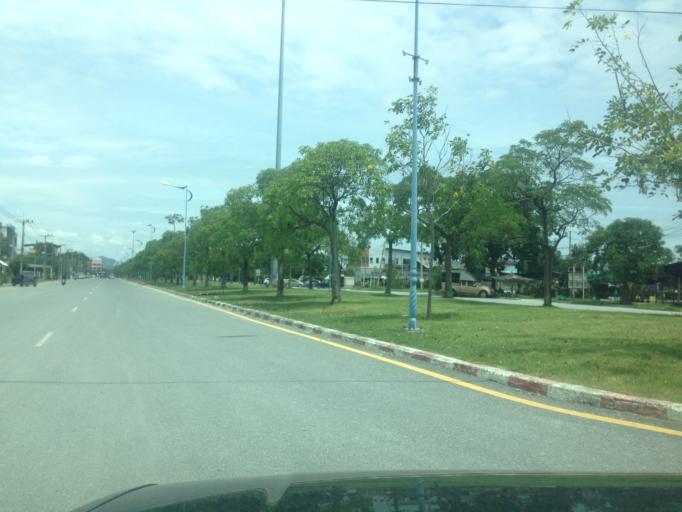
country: TH
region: Chon Buri
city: Chon Buri
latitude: 13.3430
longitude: 100.9500
